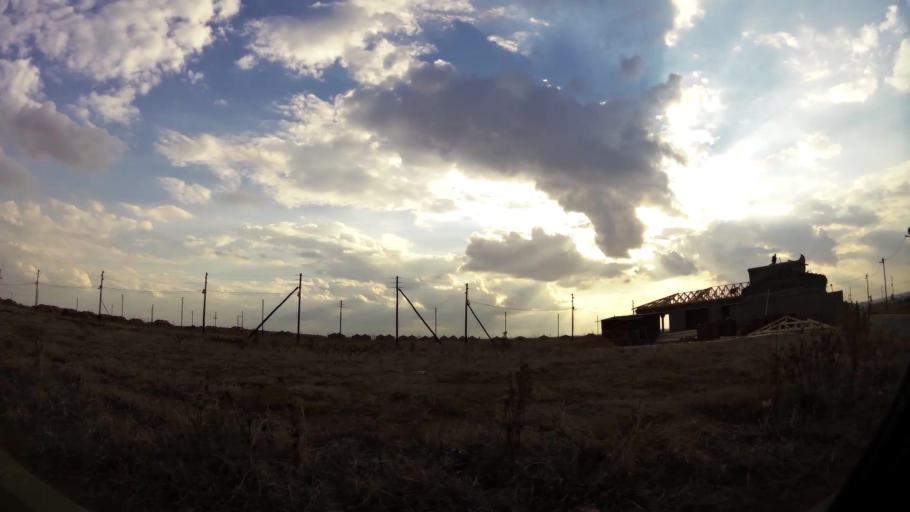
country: ZA
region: Gauteng
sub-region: Sedibeng District Municipality
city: Vanderbijlpark
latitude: -26.6109
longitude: 27.8118
